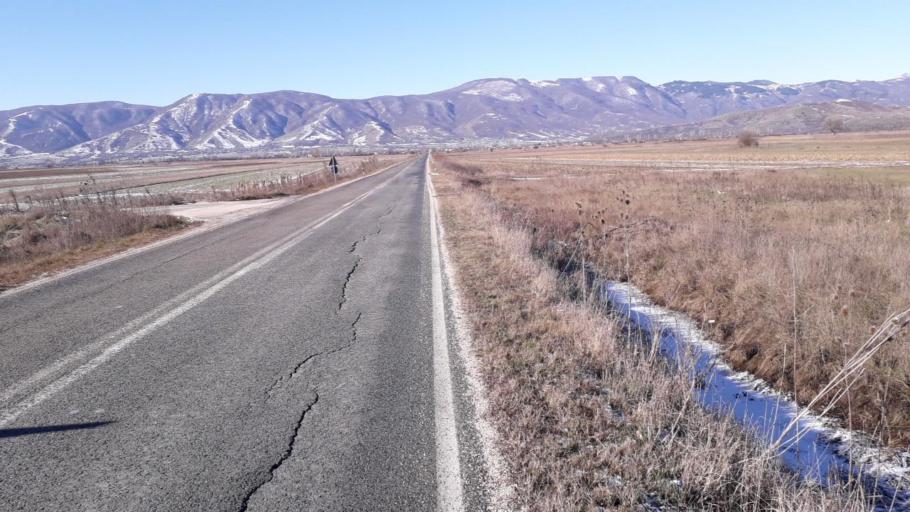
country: MK
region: Krivogastani
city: Krivogashtani
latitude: 41.3363
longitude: 21.3661
